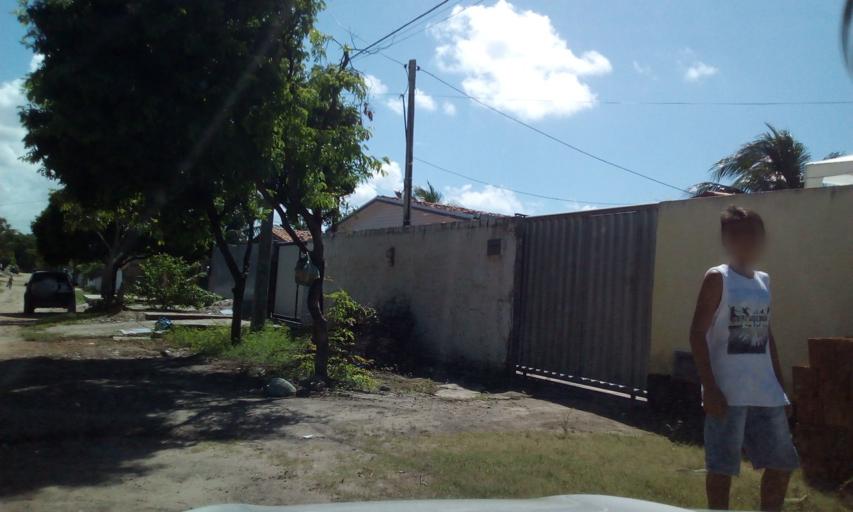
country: BR
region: Paraiba
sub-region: Joao Pessoa
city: Joao Pessoa
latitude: -7.1818
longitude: -34.8190
